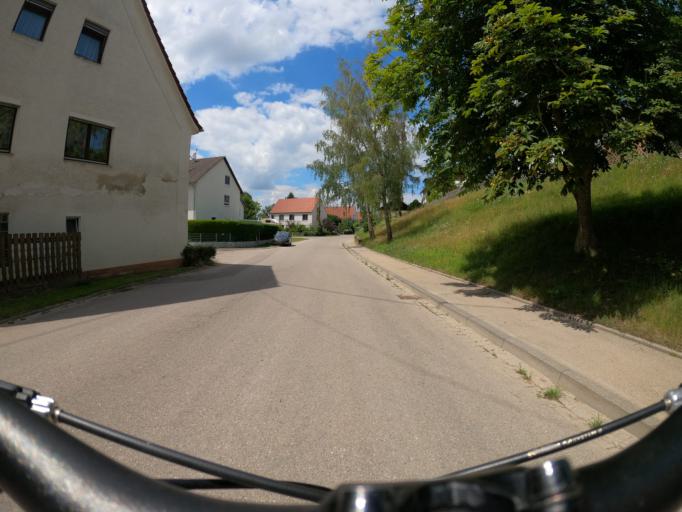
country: DE
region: Bavaria
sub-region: Swabia
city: Pfaffenhofen an der Roth
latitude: 48.3772
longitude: 10.1493
